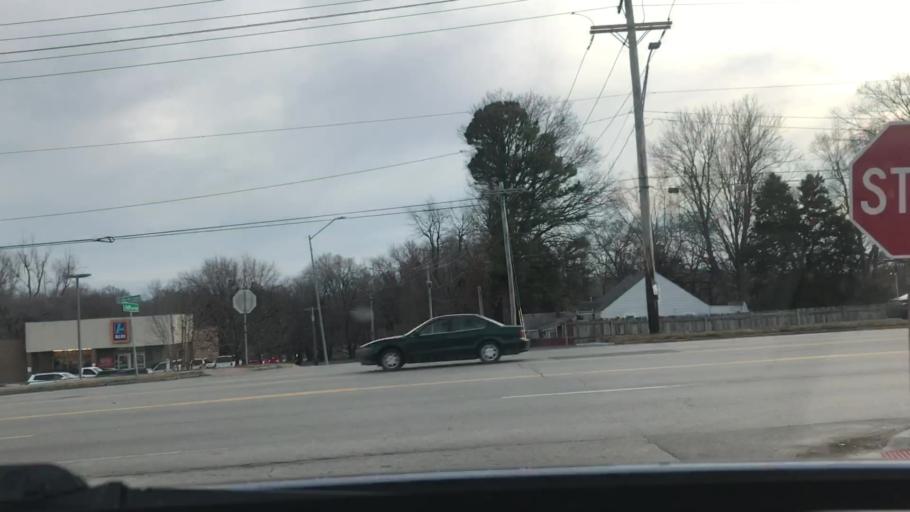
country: US
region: Missouri
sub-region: Jackson County
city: Independence
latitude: 39.0803
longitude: -94.4398
